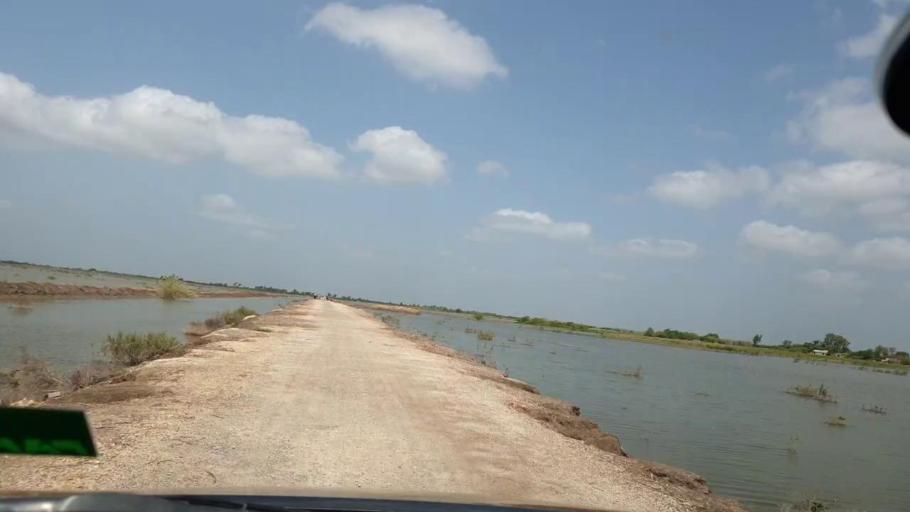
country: PK
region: Sindh
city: Kadhan
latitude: 24.5929
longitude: 69.1336
